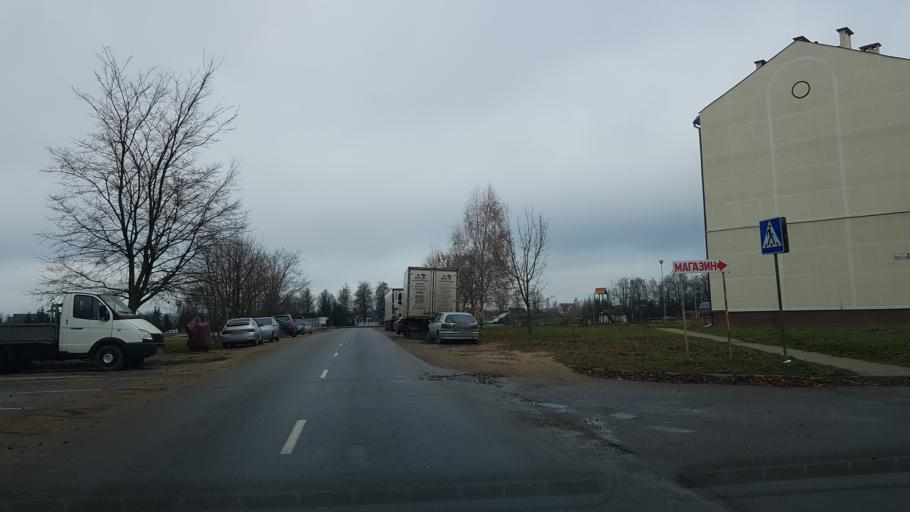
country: BY
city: Fanipol
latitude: 53.7506
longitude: 27.3282
